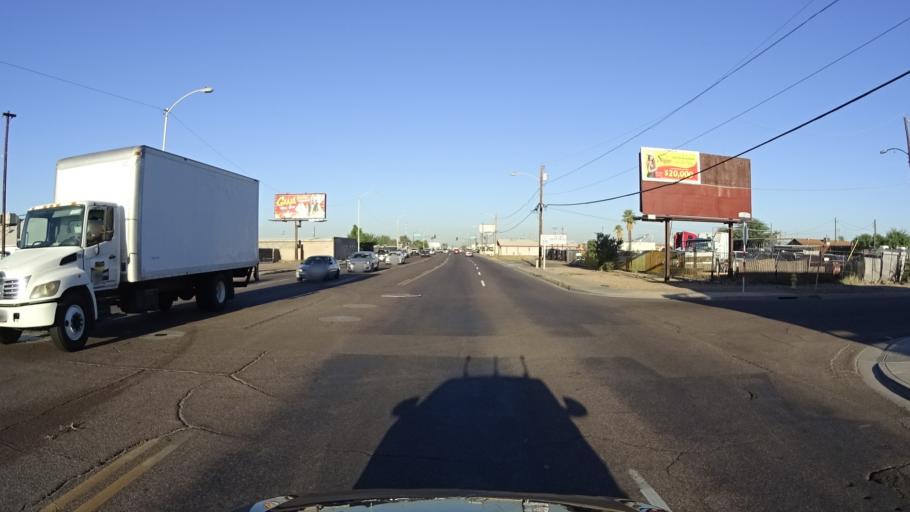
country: US
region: Arizona
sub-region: Maricopa County
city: Phoenix
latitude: 33.4368
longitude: -112.0889
